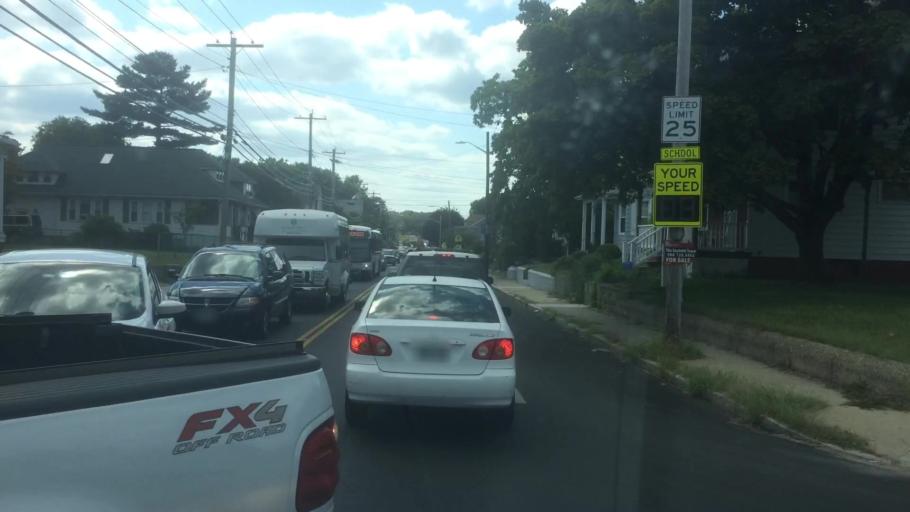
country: US
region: Rhode Island
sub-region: Providence County
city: Cranston
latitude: 41.7734
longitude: -71.4040
